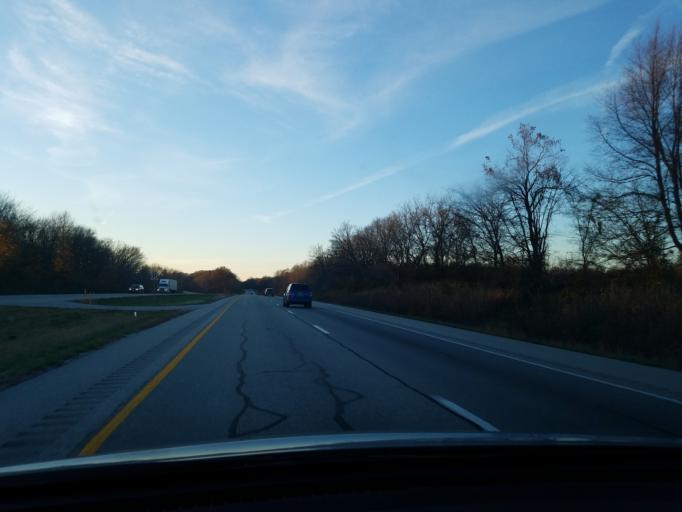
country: US
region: Indiana
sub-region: Posey County
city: Poseyville
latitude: 38.1906
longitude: -87.8340
